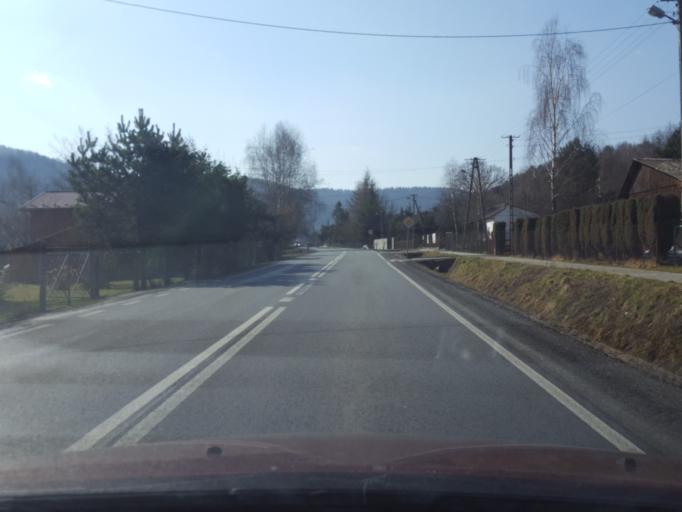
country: PL
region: Lesser Poland Voivodeship
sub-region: Powiat brzeski
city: Czchow
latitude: 49.8184
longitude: 20.6812
